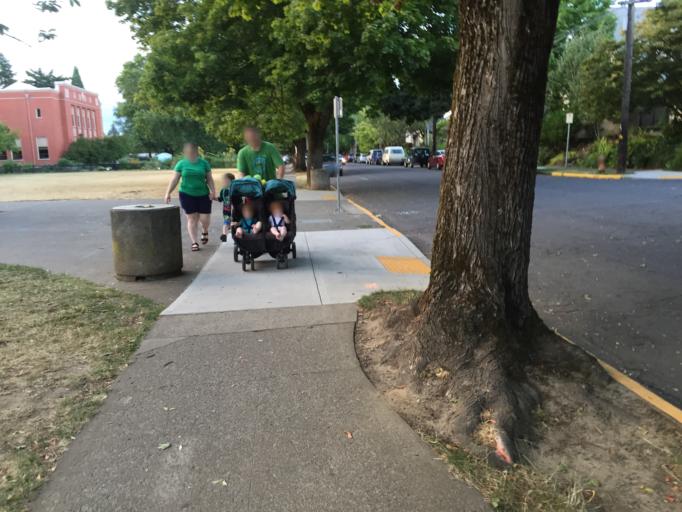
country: US
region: Oregon
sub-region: Multnomah County
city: Portland
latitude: 45.5389
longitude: -122.6261
